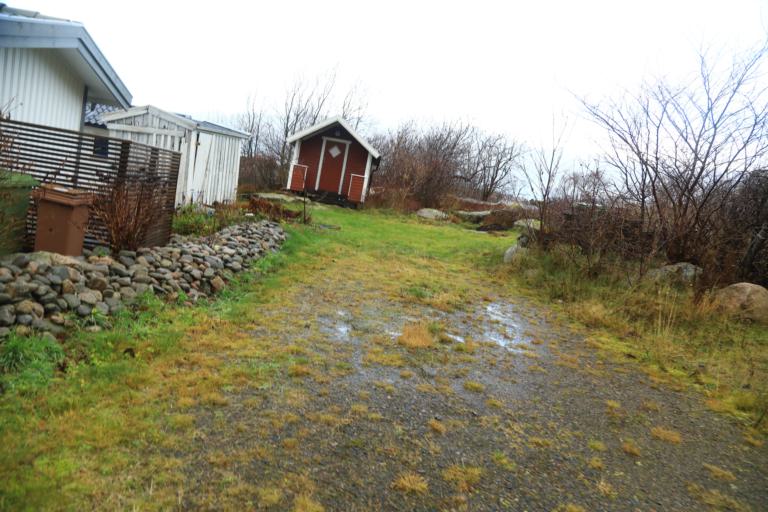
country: SE
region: Halland
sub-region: Varbergs Kommun
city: Varberg
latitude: 57.0862
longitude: 12.2580
